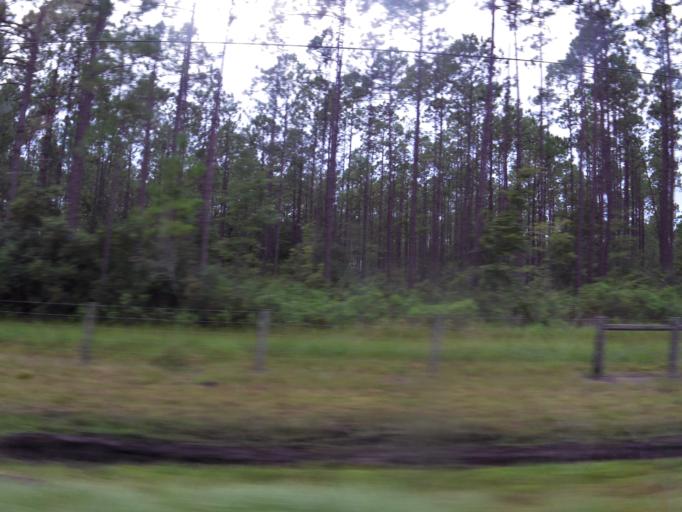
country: US
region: Florida
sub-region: Duval County
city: Baldwin
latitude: 30.3540
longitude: -81.9140
